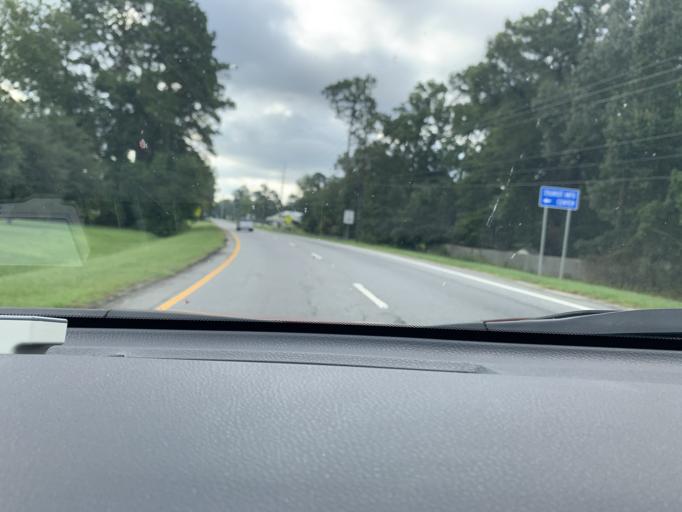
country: US
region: Georgia
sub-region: Chatham County
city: Pooler
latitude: 32.1168
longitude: -81.2548
